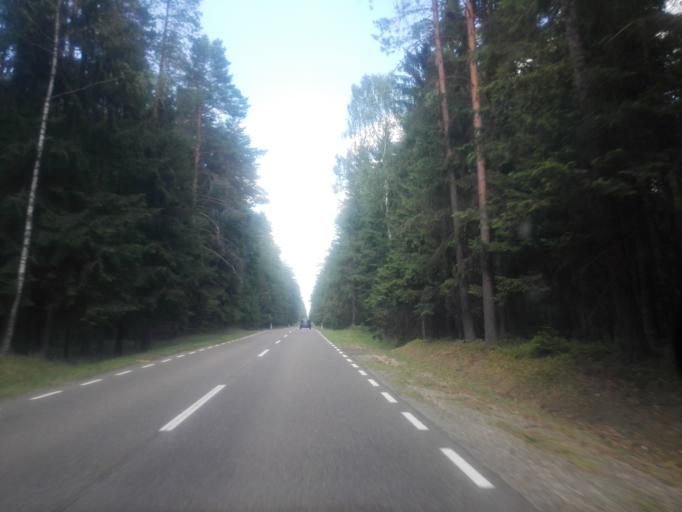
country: PL
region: Podlasie
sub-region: Powiat augustowski
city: Augustow
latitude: 53.9171
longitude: 23.1478
